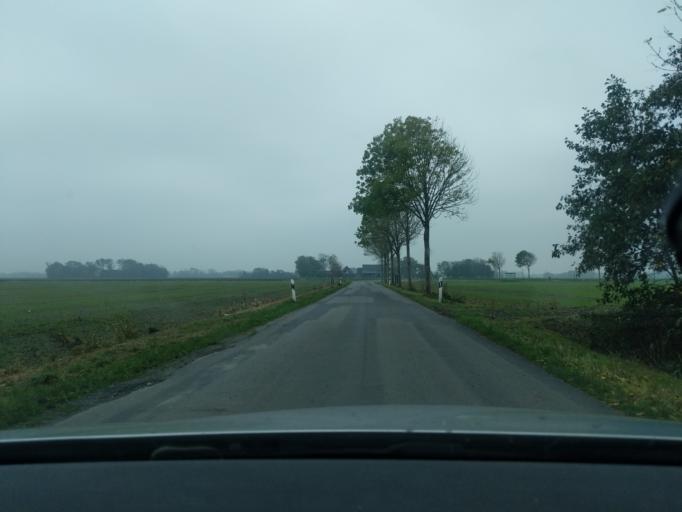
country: DE
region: Lower Saxony
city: Nordleda
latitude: 53.8244
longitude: 8.8053
